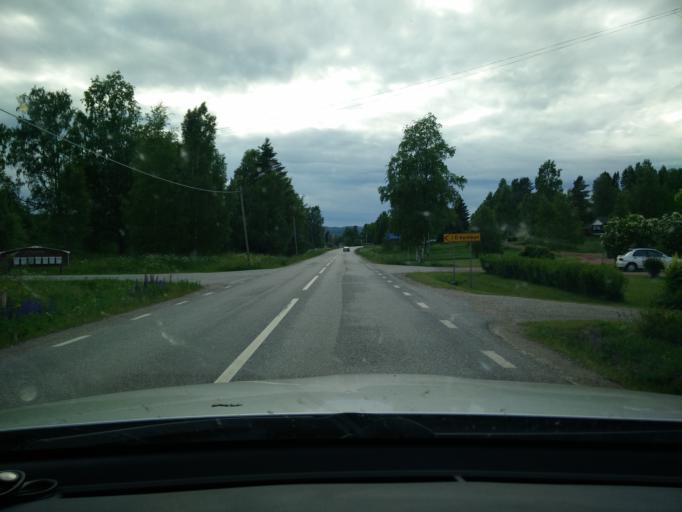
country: SE
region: Gaevleborg
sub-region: Nordanstigs Kommun
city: Bergsjoe
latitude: 62.0995
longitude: 16.7383
